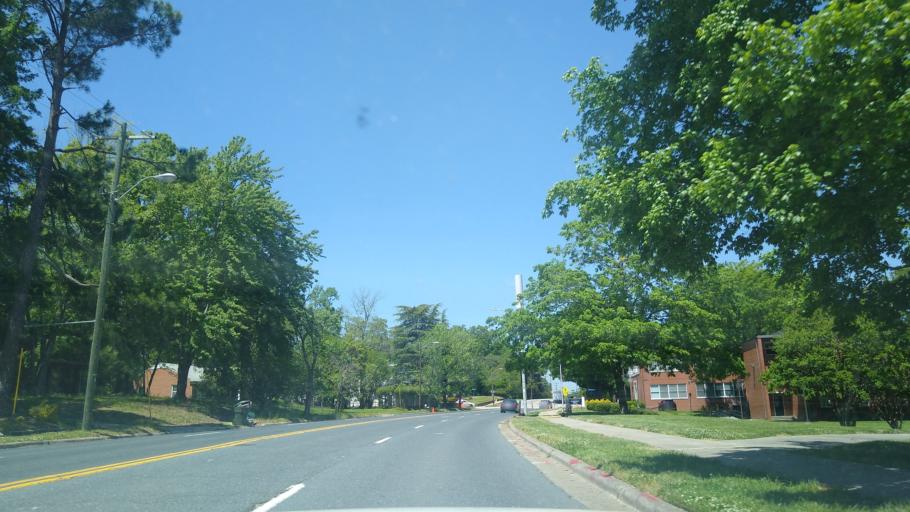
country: US
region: North Carolina
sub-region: Guilford County
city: Greensboro
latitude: 36.0727
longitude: -79.7786
